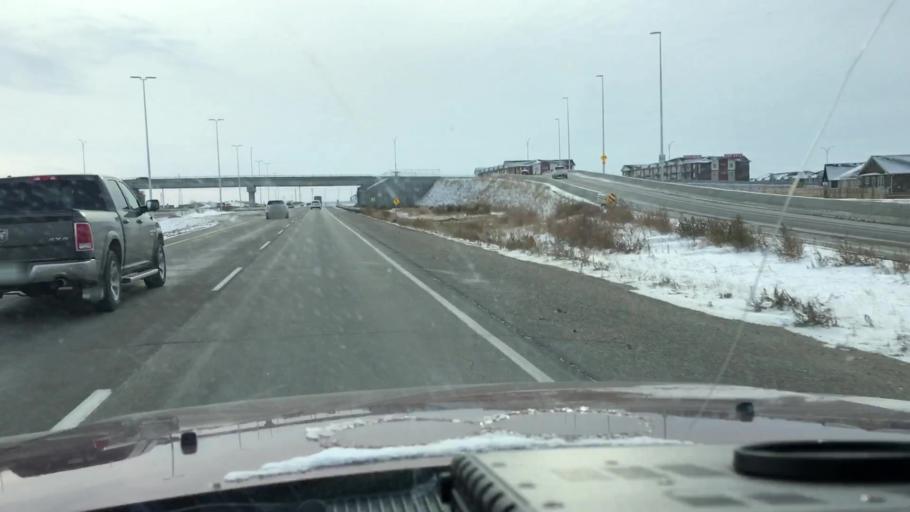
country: CA
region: Saskatchewan
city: Saskatoon
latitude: 52.0804
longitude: -106.6050
